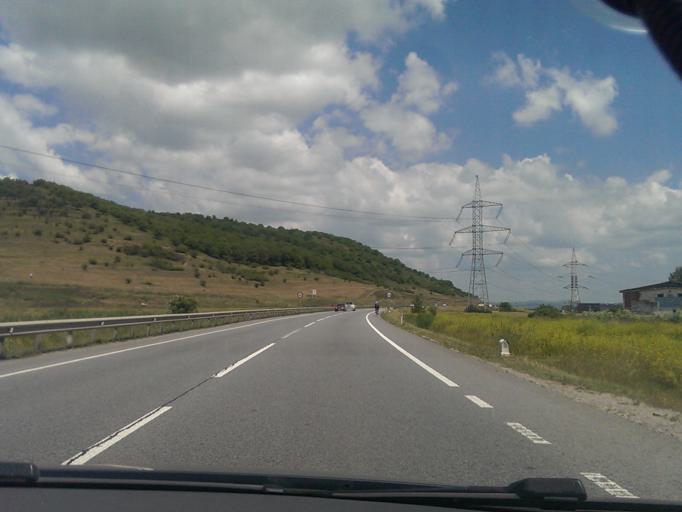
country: RO
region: Cluj
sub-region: Comuna Apahida
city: Apahida
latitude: 46.8130
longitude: 23.7368
